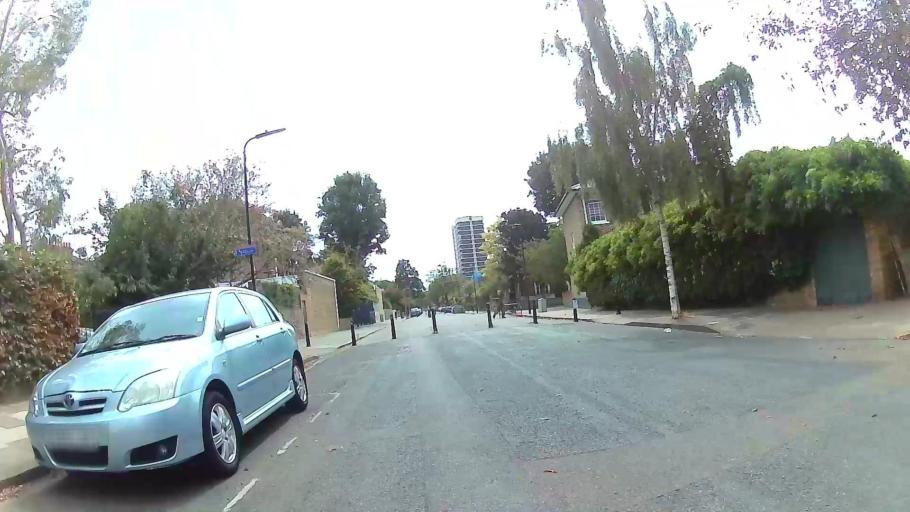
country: GB
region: England
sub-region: Greater London
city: Islington
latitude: 51.5416
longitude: -0.0818
